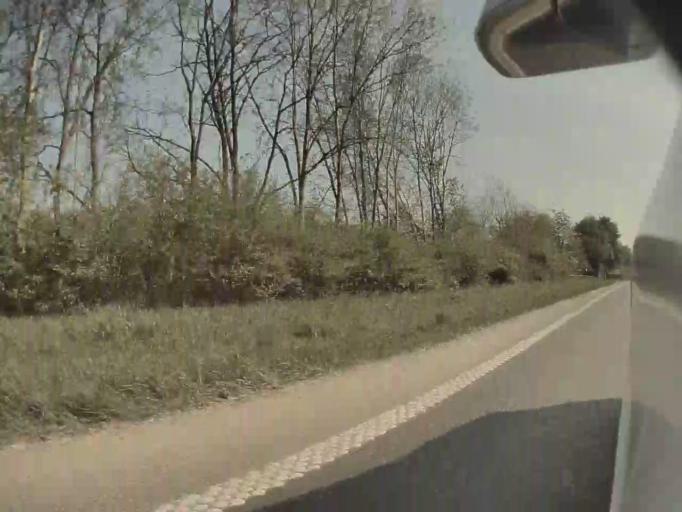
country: BE
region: Wallonia
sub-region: Province de Namur
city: Ciney
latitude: 50.3044
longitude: 5.1216
